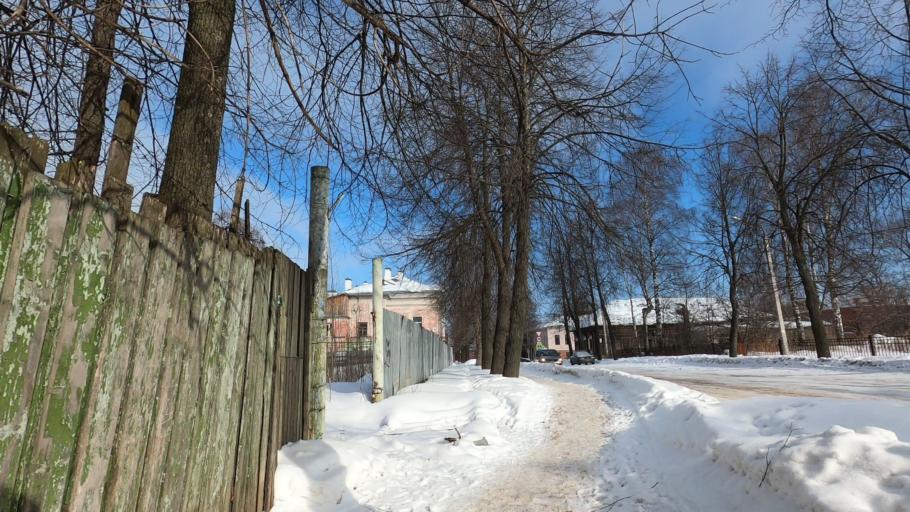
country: RU
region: Jaroslavl
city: Rybinsk
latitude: 58.0481
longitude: 38.8466
